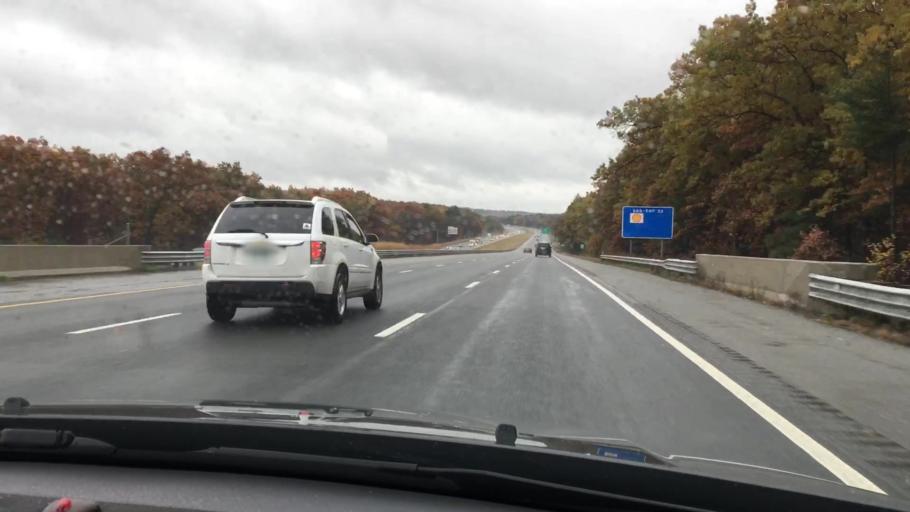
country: US
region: Massachusetts
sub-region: Middlesex County
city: Tyngsboro
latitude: 42.6440
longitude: -71.4164
